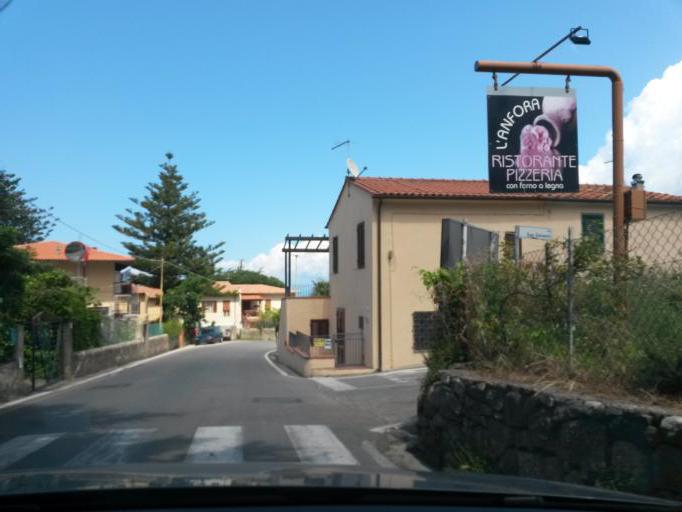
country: IT
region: Tuscany
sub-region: Provincia di Livorno
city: Marciana Marina
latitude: 42.8007
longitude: 10.1927
